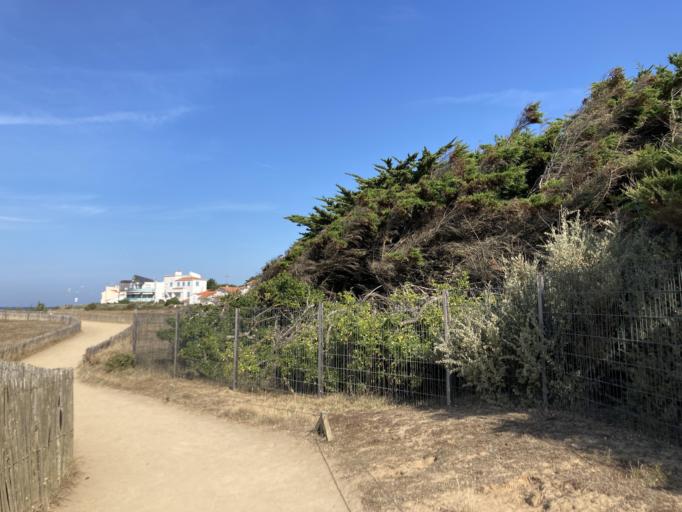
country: FR
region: Pays de la Loire
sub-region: Departement de la Vendee
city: Saint-Gilles-Croix-de-Vie
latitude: 46.6924
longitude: -1.9638
